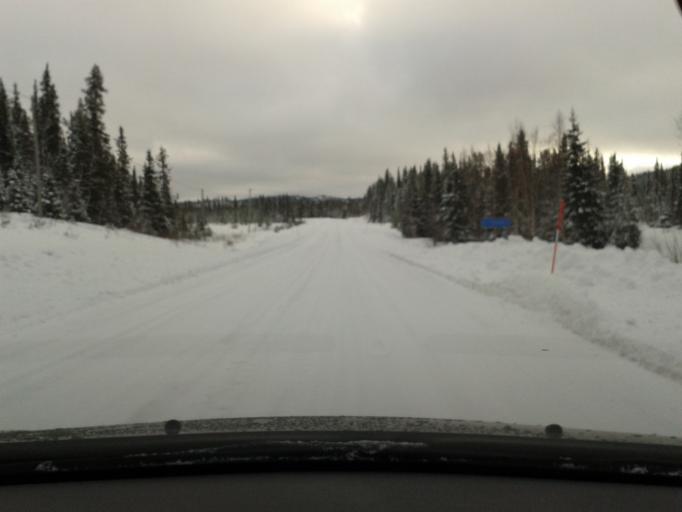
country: SE
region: Vaesterbotten
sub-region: Vilhelmina Kommun
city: Sjoberg
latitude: 65.2461
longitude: 15.7452
